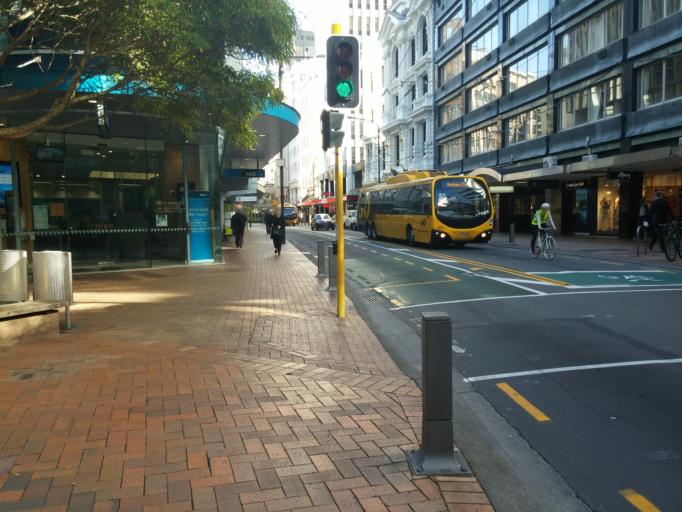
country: NZ
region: Wellington
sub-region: Wellington City
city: Wellington
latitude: -41.2848
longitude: 174.7755
